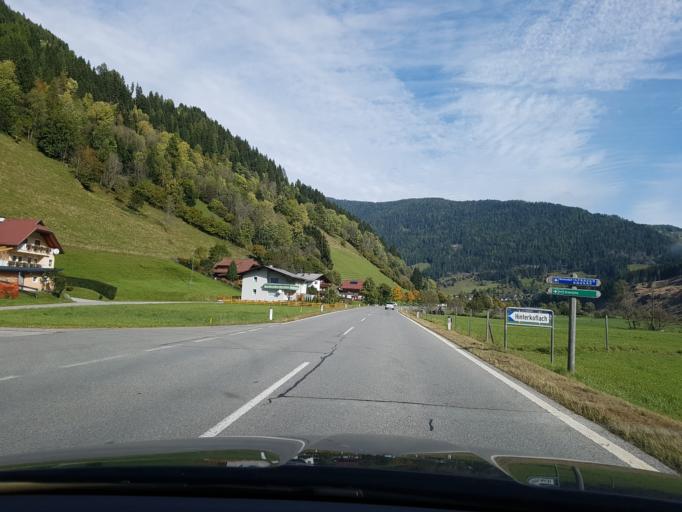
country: AT
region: Carinthia
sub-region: Politischer Bezirk Spittal an der Drau
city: Kleinkirchheim
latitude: 46.8446
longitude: 13.8811
